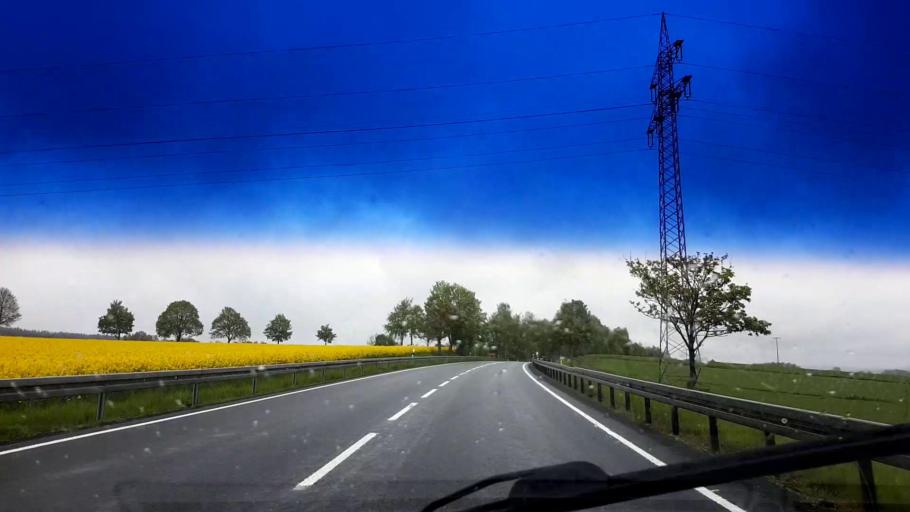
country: DE
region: Bavaria
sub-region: Upper Franconia
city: Arzberg
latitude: 50.0724
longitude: 12.1891
